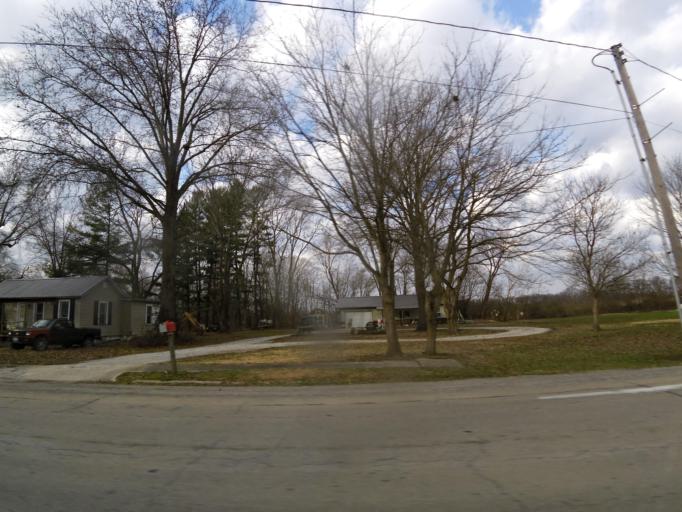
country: US
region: Illinois
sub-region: Fayette County
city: Ramsey
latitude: 39.1489
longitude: -89.1083
